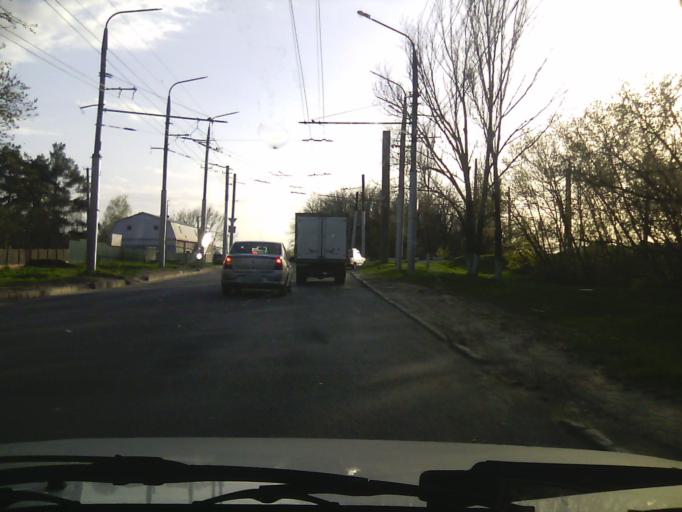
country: RU
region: Saratov
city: Sokolovyy
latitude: 51.5899
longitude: 45.9090
